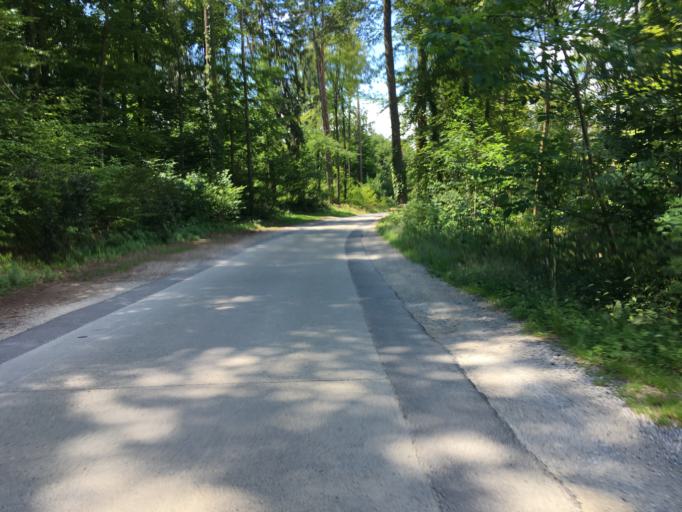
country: CH
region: Fribourg
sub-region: Broye District
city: Domdidier
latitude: 46.9218
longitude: 6.9734
